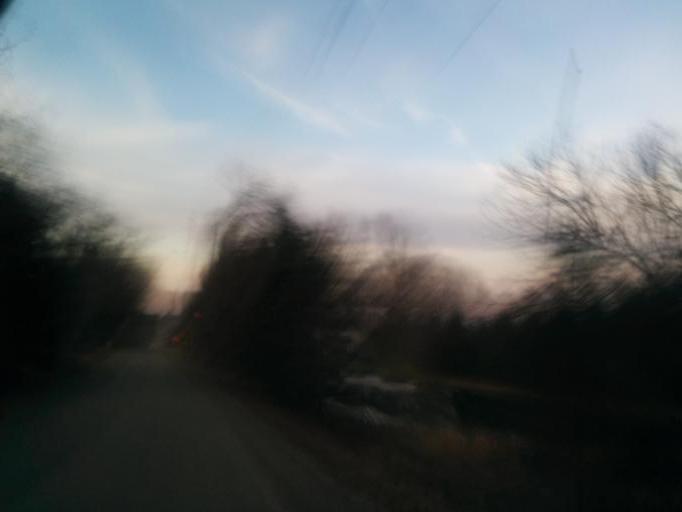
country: CA
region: Ontario
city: Orangeville
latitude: 43.9713
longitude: -79.9737
